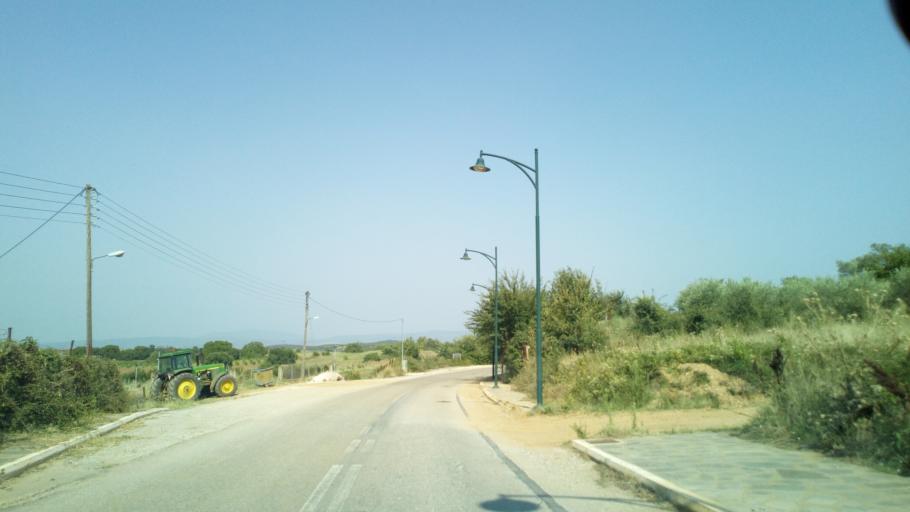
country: GR
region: Central Macedonia
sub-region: Nomos Chalkidikis
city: Galatista
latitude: 40.5129
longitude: 23.3560
